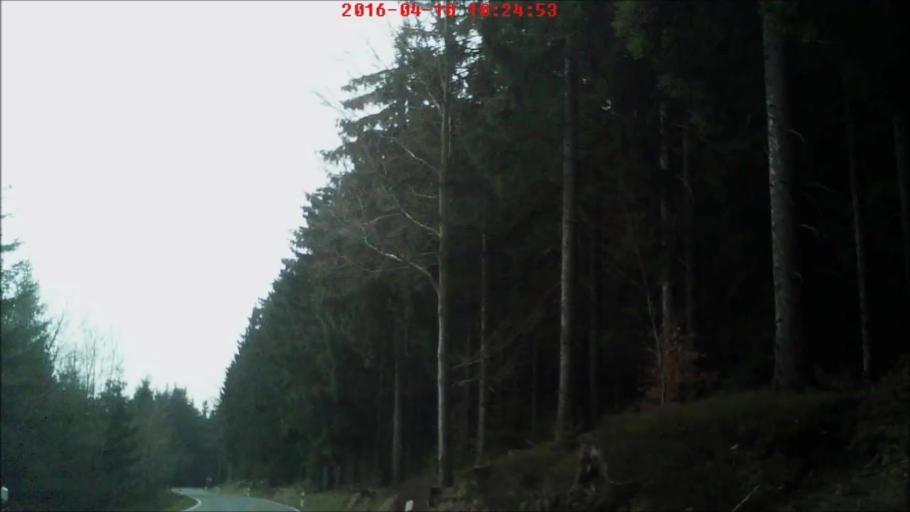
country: DE
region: Thuringia
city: Stutzerbach
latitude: 50.6470
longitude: 10.8831
